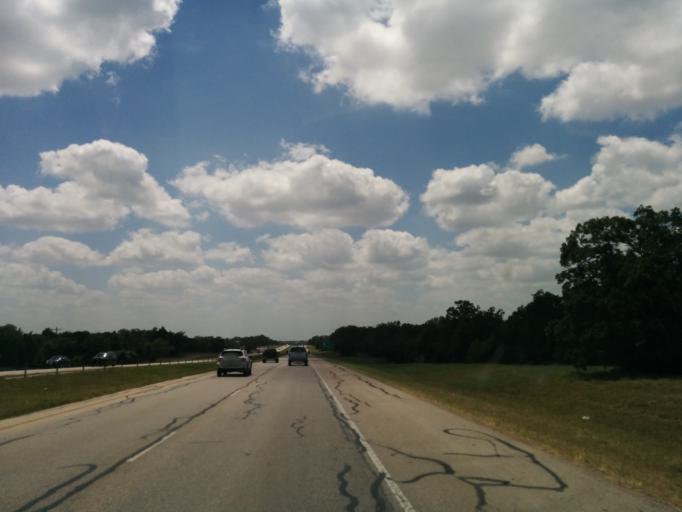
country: US
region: Texas
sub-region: Bastrop County
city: Bastrop
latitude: 30.1109
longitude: -97.3918
